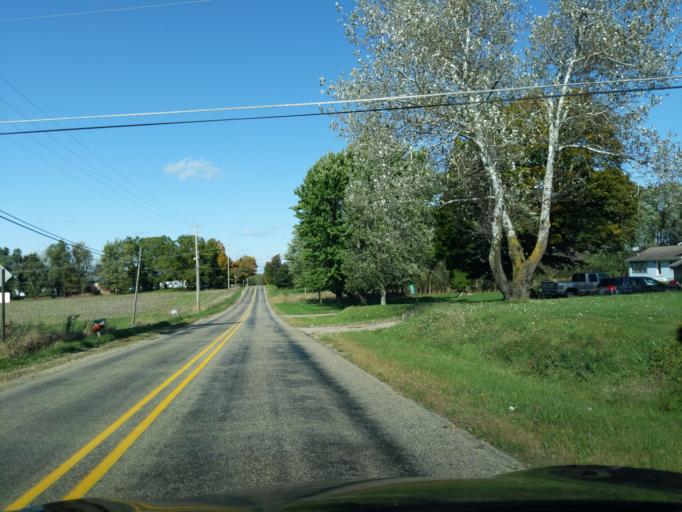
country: US
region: Michigan
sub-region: Eaton County
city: Charlotte
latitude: 42.5921
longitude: -84.7979
